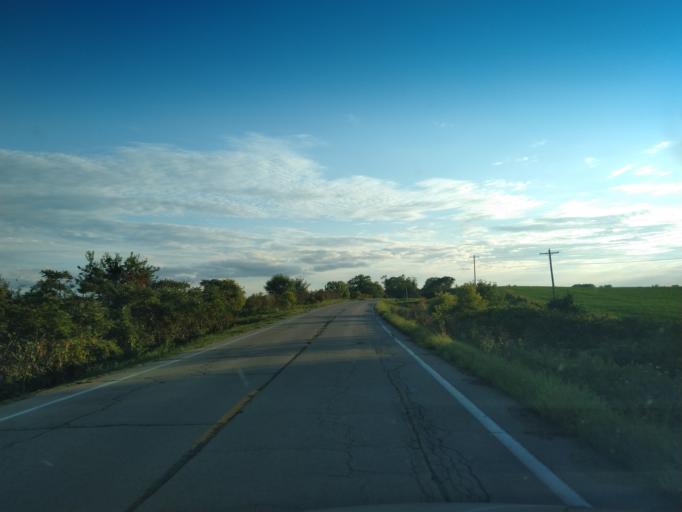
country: US
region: Iowa
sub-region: Jackson County
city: Maquoketa
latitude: 42.1467
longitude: -90.7606
